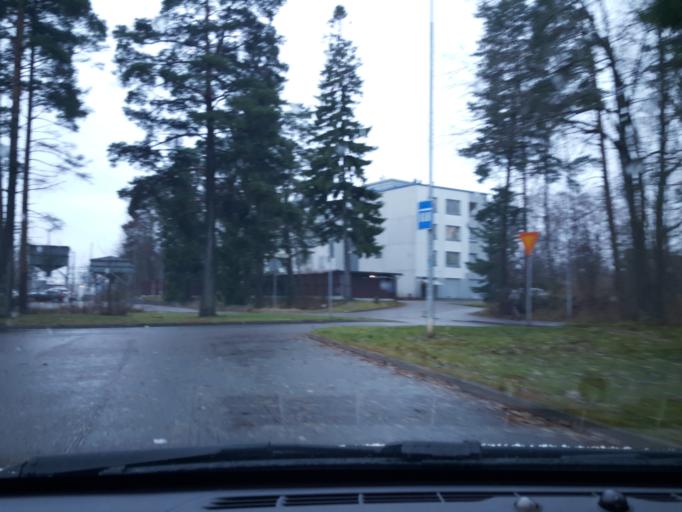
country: FI
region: Uusimaa
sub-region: Helsinki
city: Vantaa
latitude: 60.3040
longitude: 25.0490
